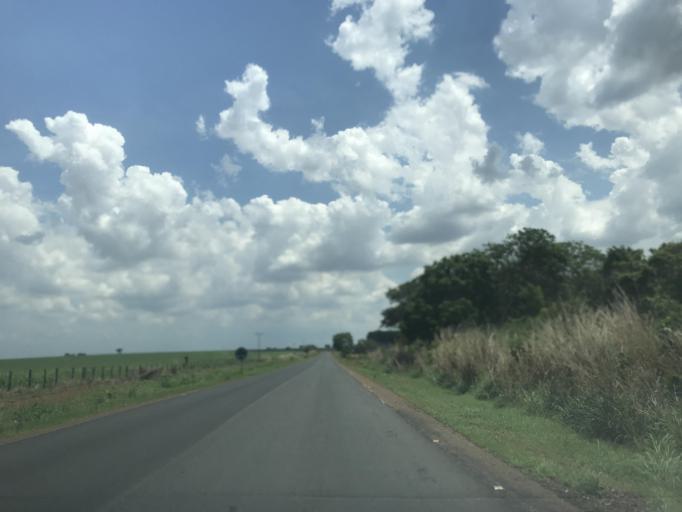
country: BR
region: Goias
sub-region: Piracanjuba
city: Piracanjuba
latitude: -17.3616
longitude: -48.7961
